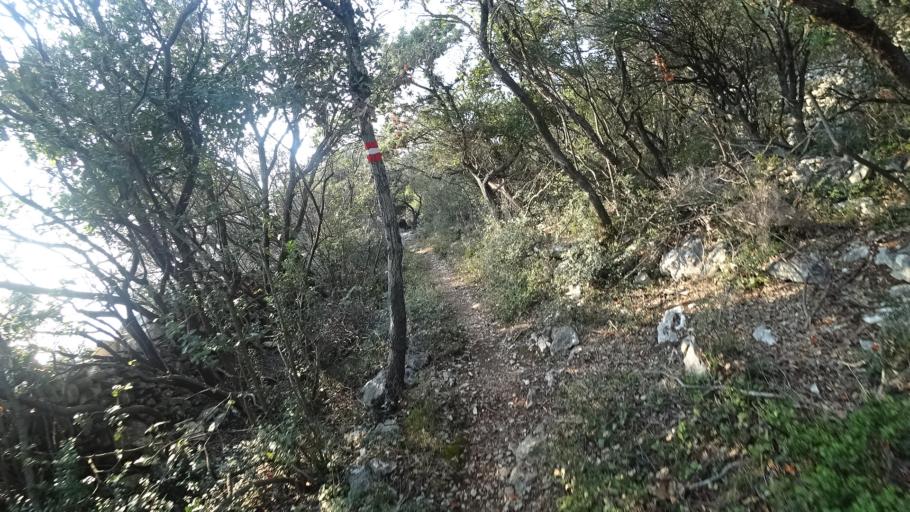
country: HR
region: Primorsko-Goranska
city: Mali Losinj
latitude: 44.5115
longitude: 14.4821
